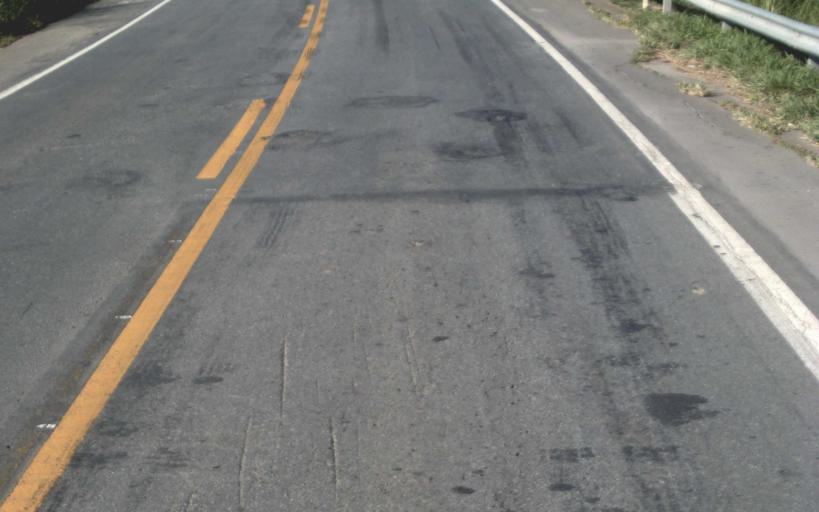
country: BR
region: Minas Gerais
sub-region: Belo Oriente
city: Belo Oriente
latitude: -19.2176
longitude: -42.3080
